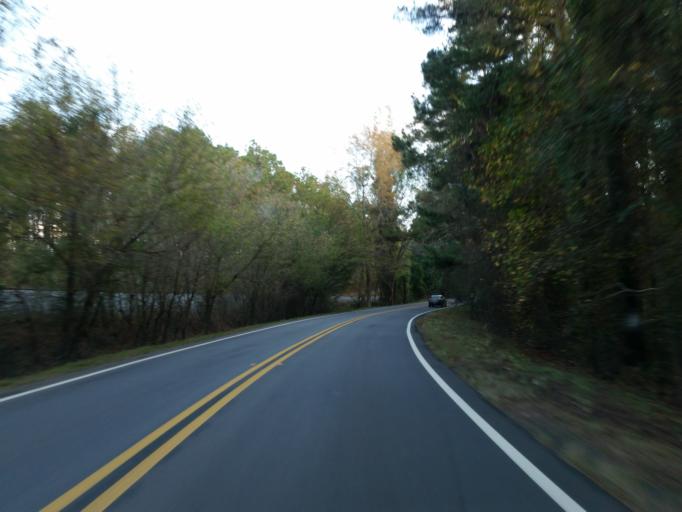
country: US
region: Georgia
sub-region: Monroe County
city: Forsyth
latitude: 32.9507
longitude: -83.8475
